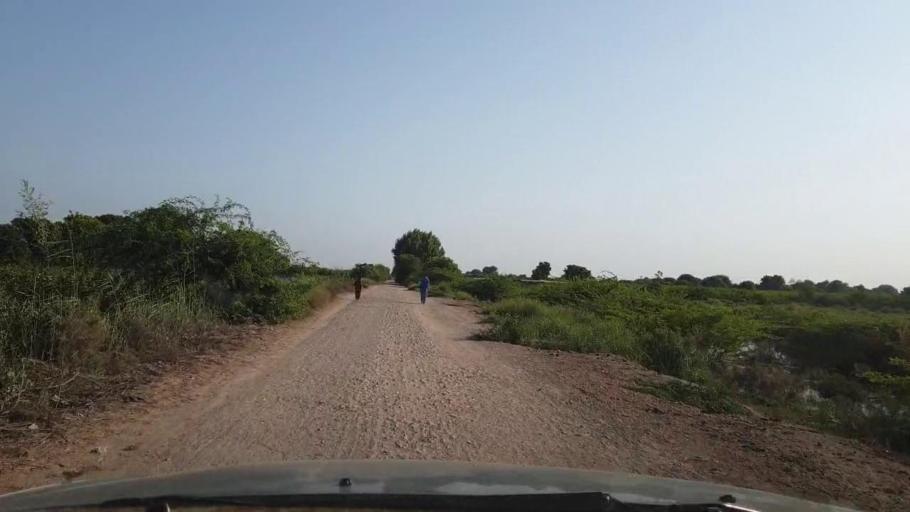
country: PK
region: Sindh
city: Tando Ghulam Ali
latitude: 25.1439
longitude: 68.9428
